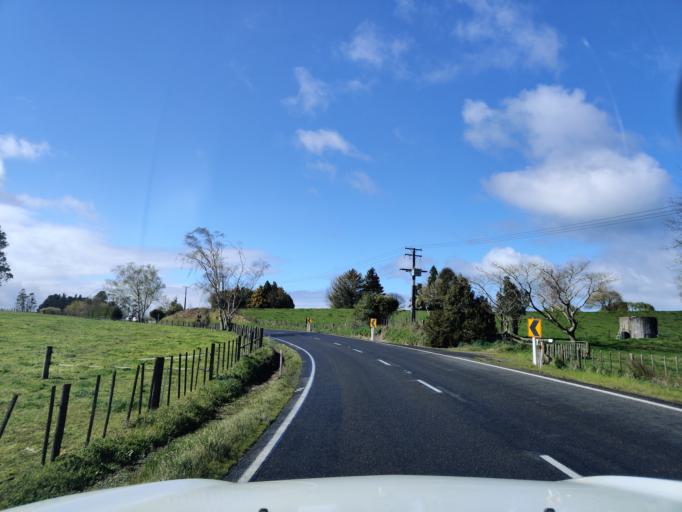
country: NZ
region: Waikato
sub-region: Otorohanga District
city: Otorohanga
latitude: -38.0720
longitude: 175.1771
